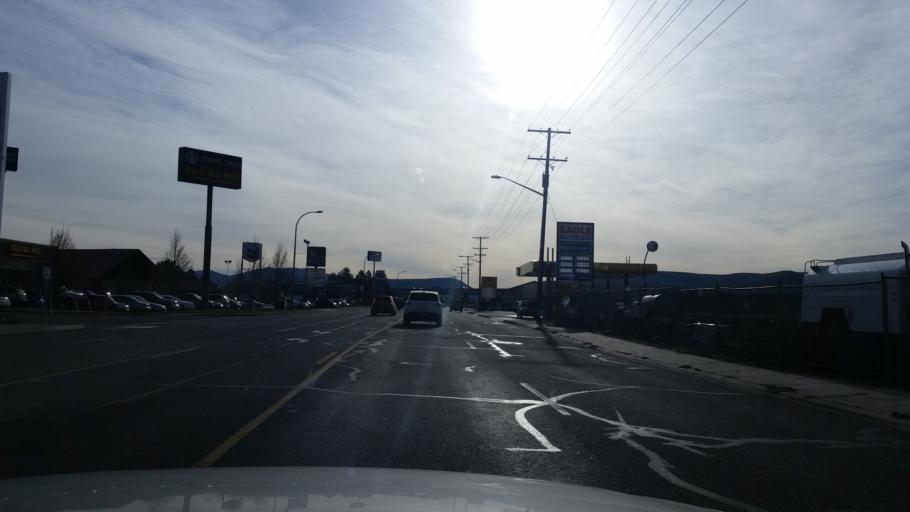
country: US
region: Washington
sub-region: Kittitas County
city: Ellensburg
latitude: 46.9773
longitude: -120.5432
